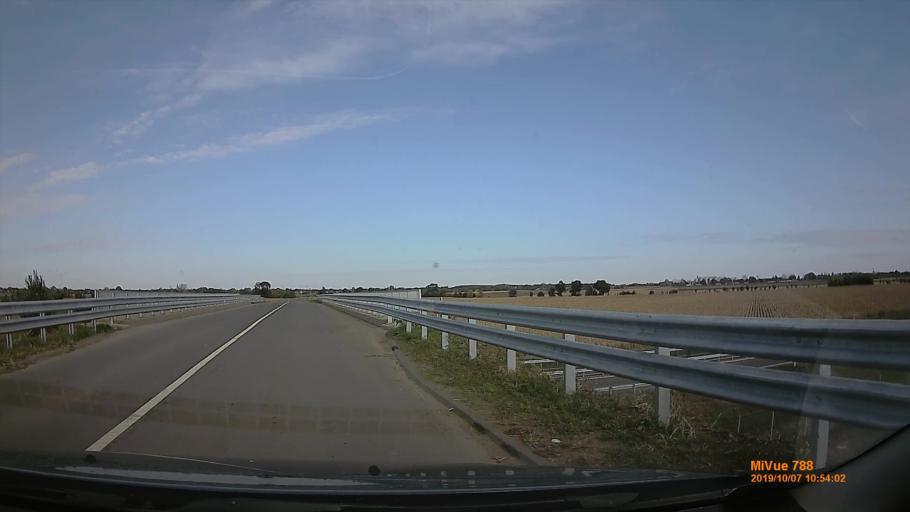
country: HU
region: Bekes
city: Kondoros
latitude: 46.7376
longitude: 20.8087
